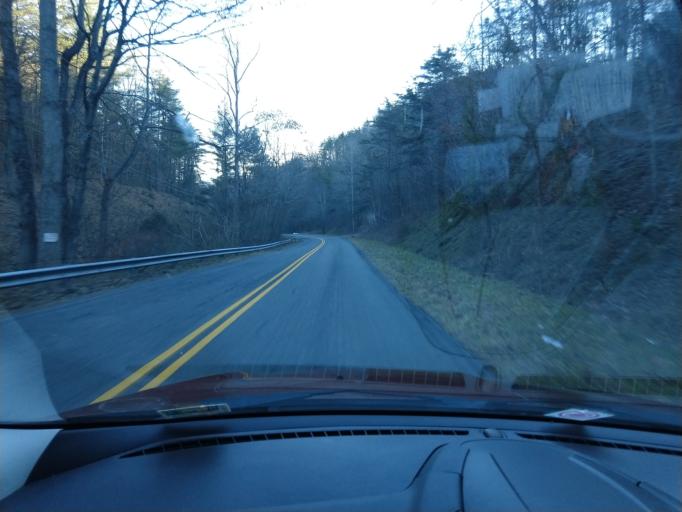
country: US
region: Virginia
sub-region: Alleghany County
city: Clifton Forge
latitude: 37.8385
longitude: -79.8470
